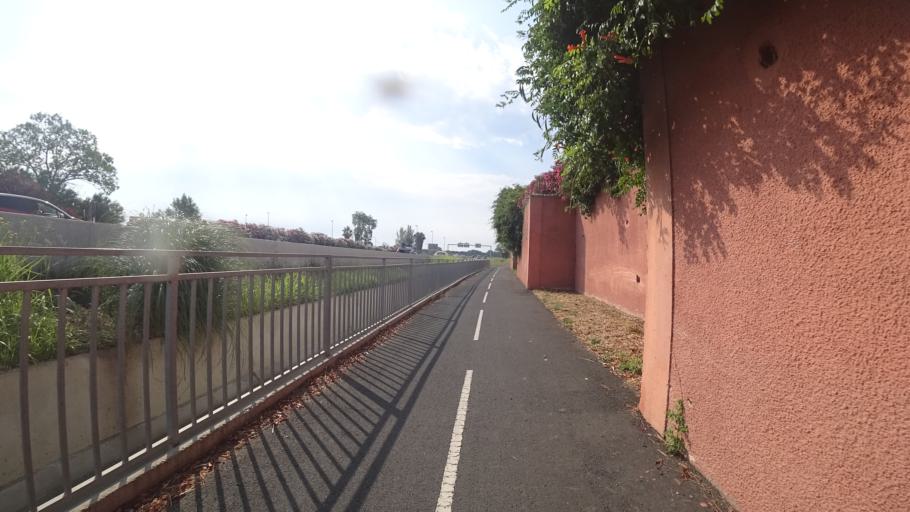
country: FR
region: Languedoc-Roussillon
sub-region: Departement des Pyrenees-Orientales
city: Canet-en-Roussillon
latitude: 42.7013
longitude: 3.0177
